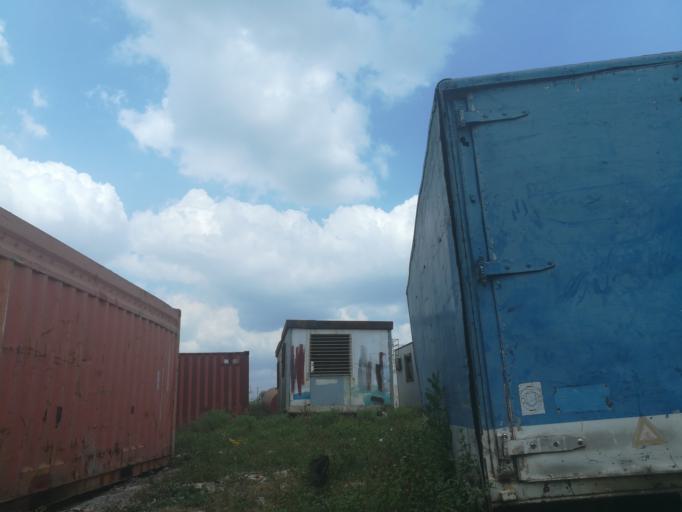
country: NG
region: Abuja Federal Capital Territory
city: Abuja
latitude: 9.0594
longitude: 7.4462
